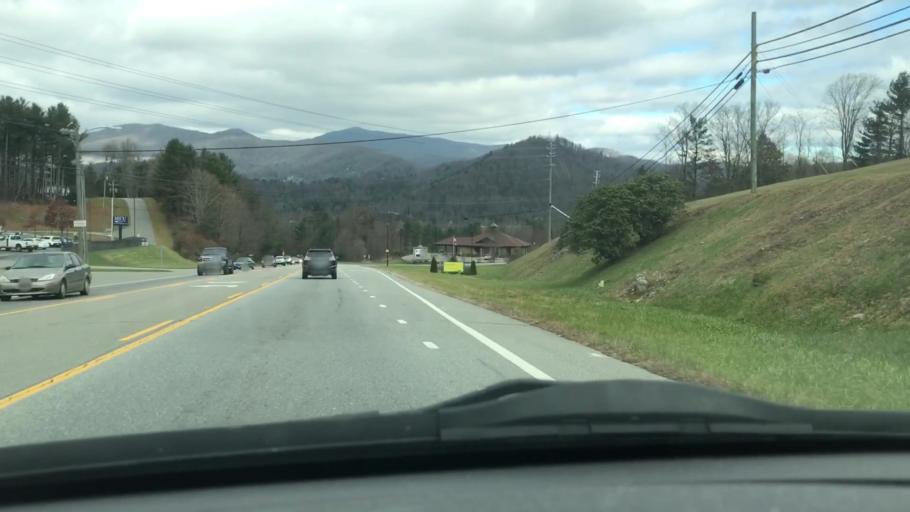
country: US
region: North Carolina
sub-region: Mitchell County
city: Spruce Pine
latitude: 35.9037
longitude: -82.0742
